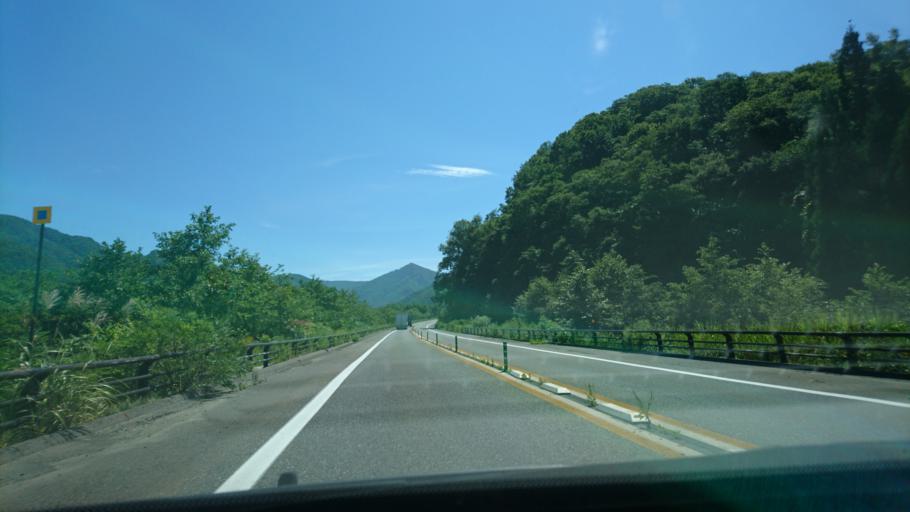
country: JP
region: Iwate
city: Tono
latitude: 39.2625
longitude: 141.6104
